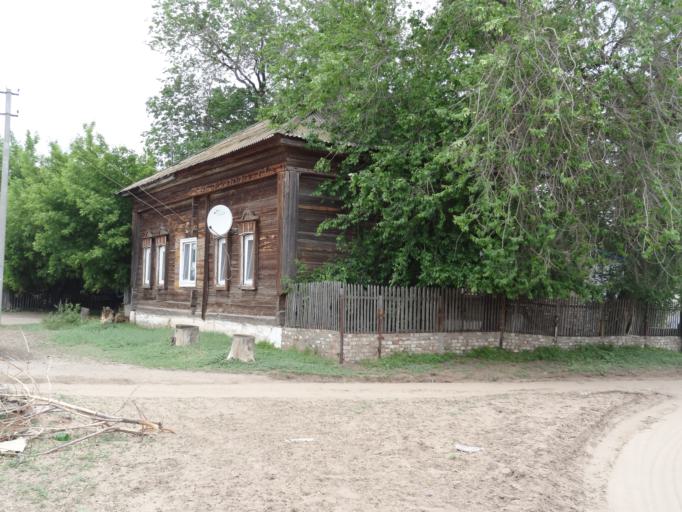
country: RU
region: Saratov
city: Privolzhskiy
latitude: 51.1812
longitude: 45.9174
